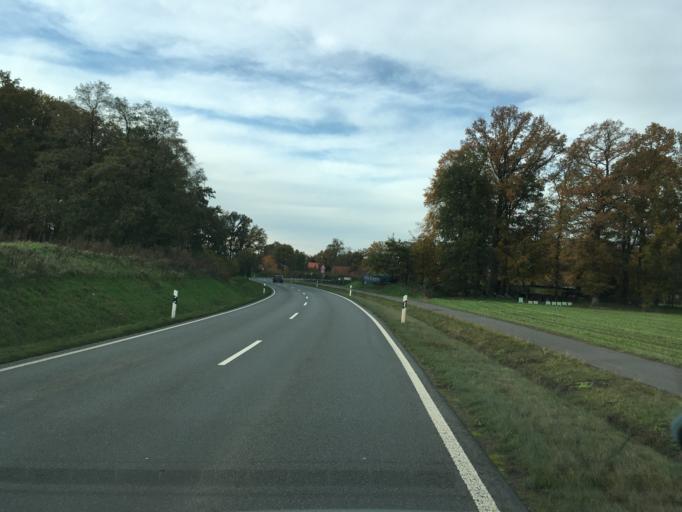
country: DE
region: North Rhine-Westphalia
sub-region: Regierungsbezirk Munster
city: Heiden
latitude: 51.8823
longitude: 6.9078
